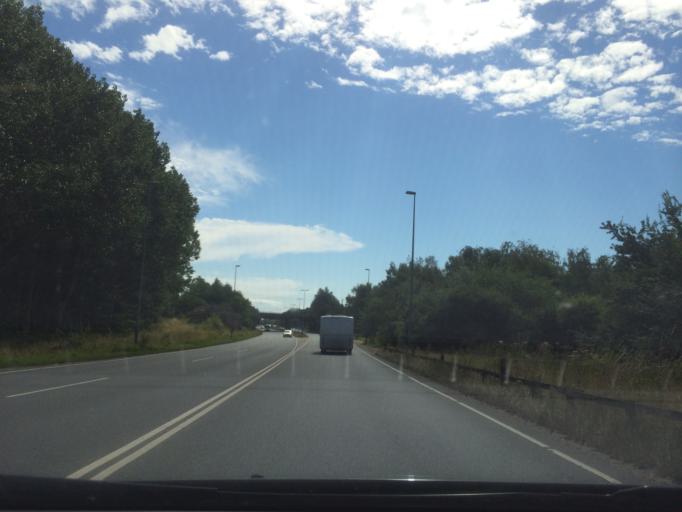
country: DK
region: Zealand
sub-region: Koge Kommune
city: Koge
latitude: 55.4839
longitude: 12.1688
